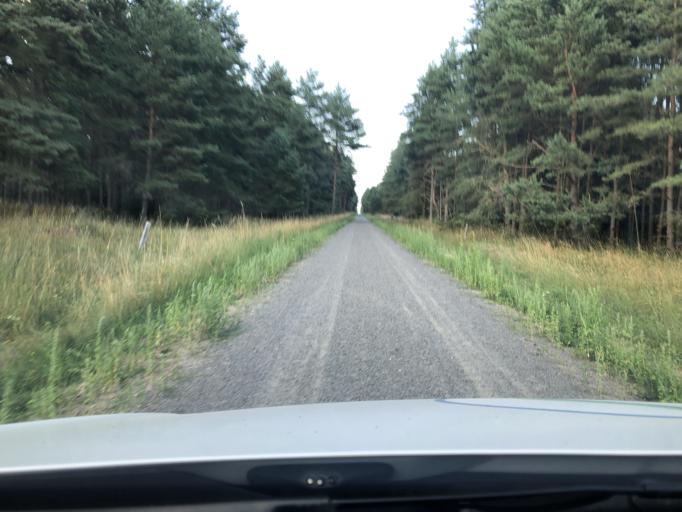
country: SE
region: Skane
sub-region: Kristianstads Kommun
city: Norra Asum
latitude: 55.9235
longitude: 14.1257
